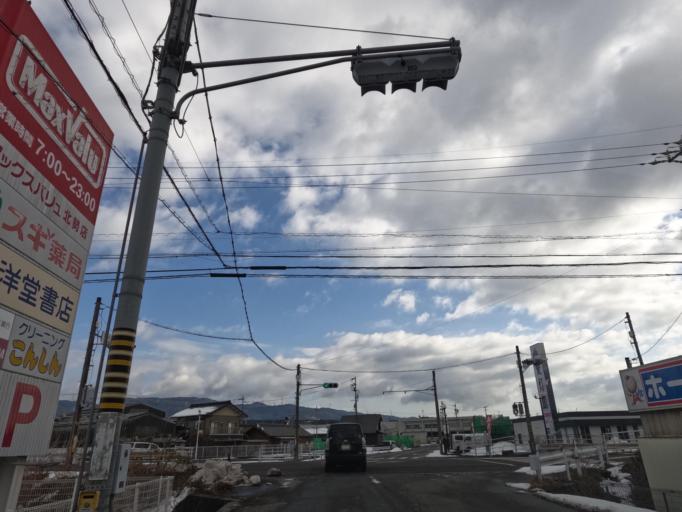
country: JP
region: Mie
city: Komono
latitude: 35.1539
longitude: 136.5102
